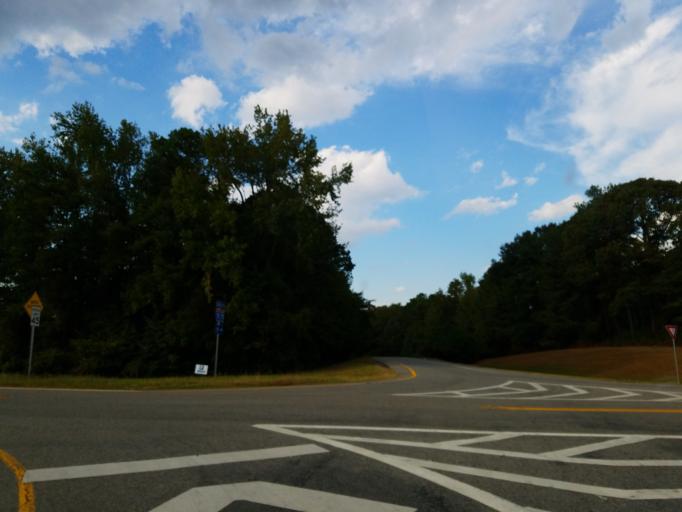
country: US
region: Georgia
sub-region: Monroe County
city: Forsyth
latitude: 33.1122
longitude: -84.0018
